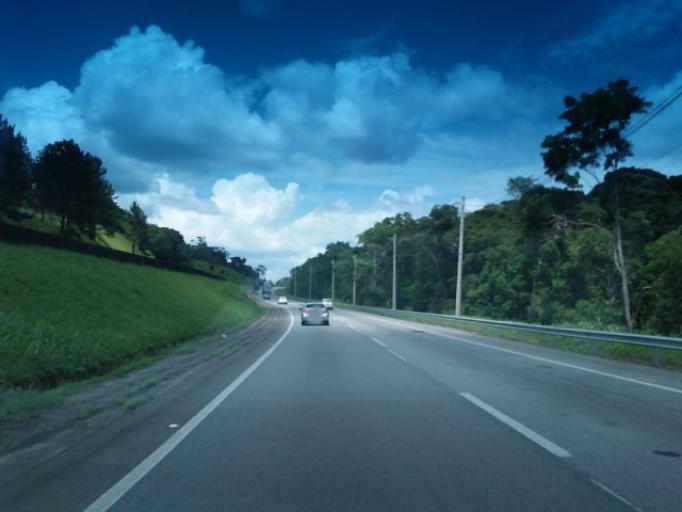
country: BR
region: Sao Paulo
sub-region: Juquitiba
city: Juquitiba
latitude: -23.9577
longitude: -47.1144
